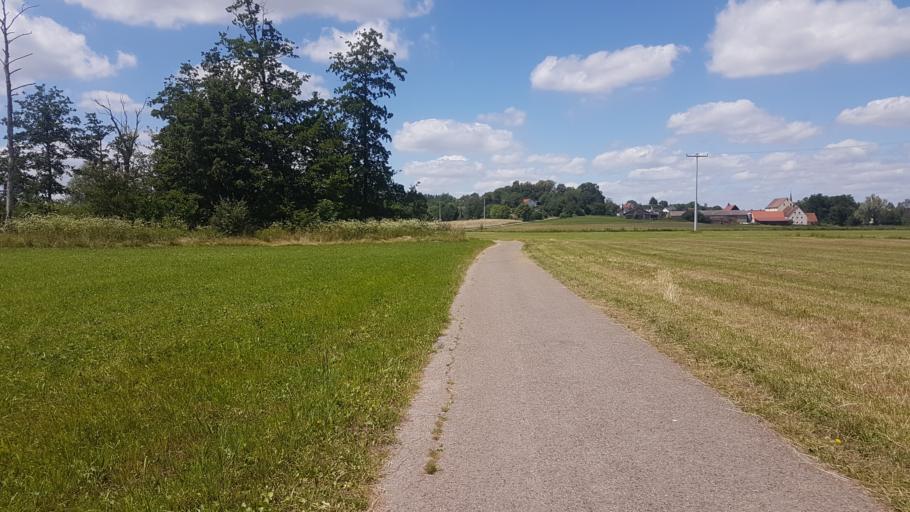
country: DE
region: Bavaria
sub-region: Regierungsbezirk Mittelfranken
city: Leutershausen
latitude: 49.3064
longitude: 10.3963
